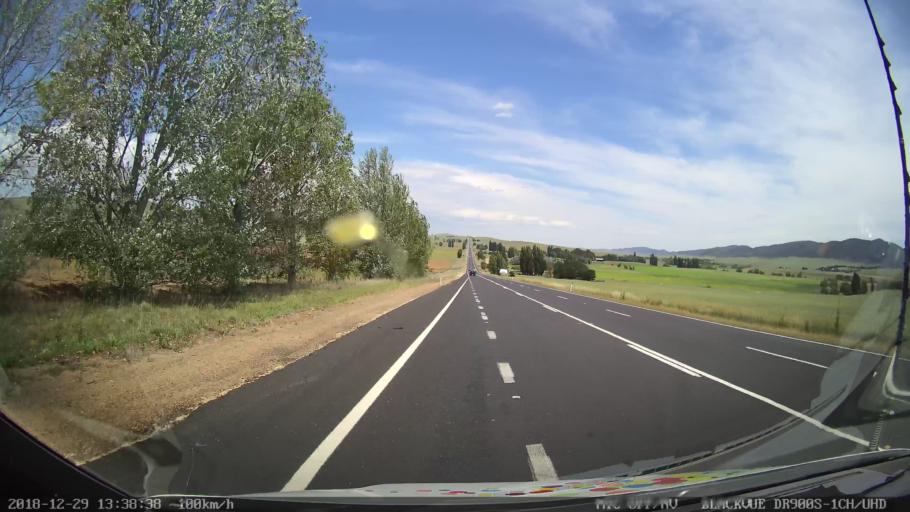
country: AU
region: New South Wales
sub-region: Cooma-Monaro
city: Cooma
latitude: -36.0011
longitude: 149.1426
